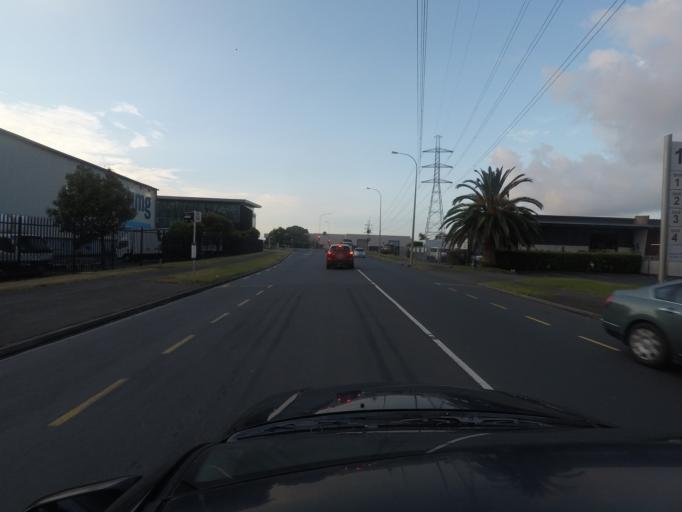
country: NZ
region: Auckland
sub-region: Auckland
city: Tamaki
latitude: -36.9369
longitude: 174.8849
